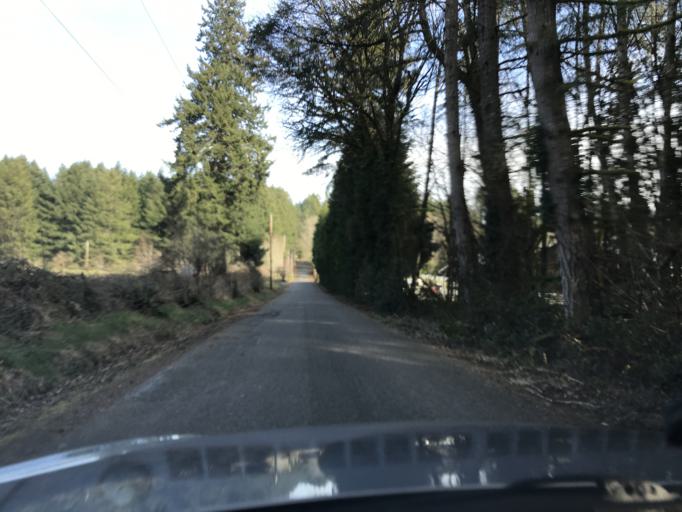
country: US
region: Washington
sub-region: Pierce County
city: Longbranch
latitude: 47.2246
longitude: -122.7954
